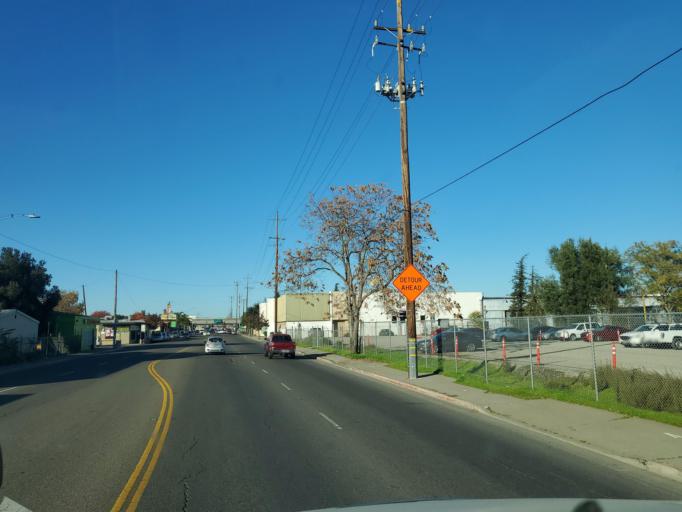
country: US
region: California
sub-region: San Joaquin County
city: Stockton
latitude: 37.9502
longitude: -121.2700
